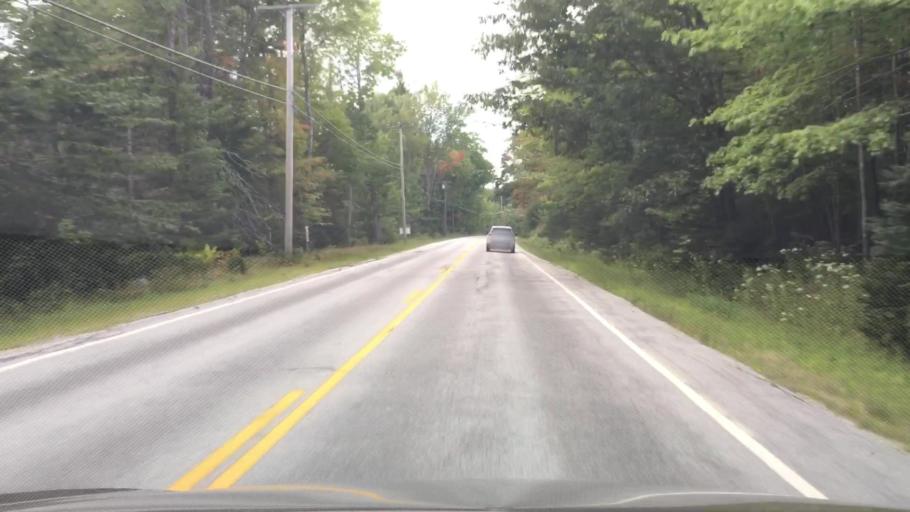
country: US
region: Maine
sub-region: Hancock County
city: Penobscot
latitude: 44.4305
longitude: -68.6050
